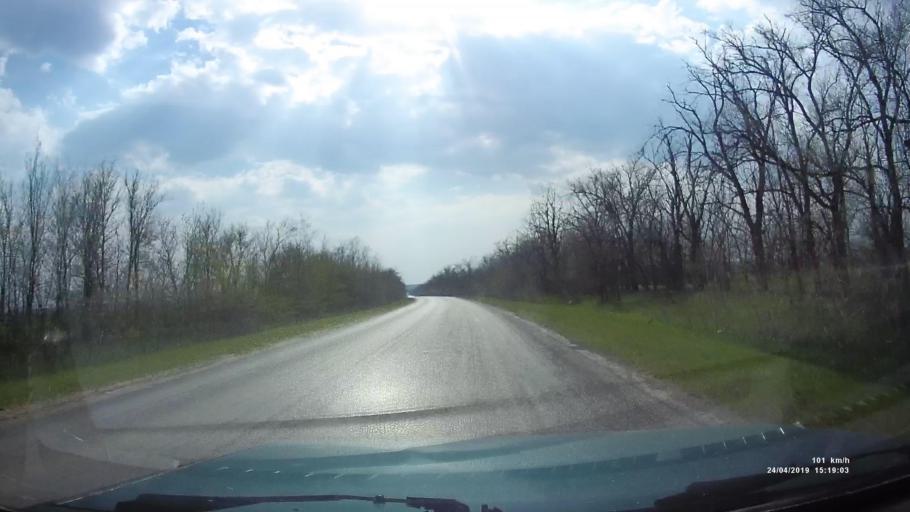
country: RU
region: Rostov
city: Remontnoye
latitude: 46.5427
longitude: 43.1540
